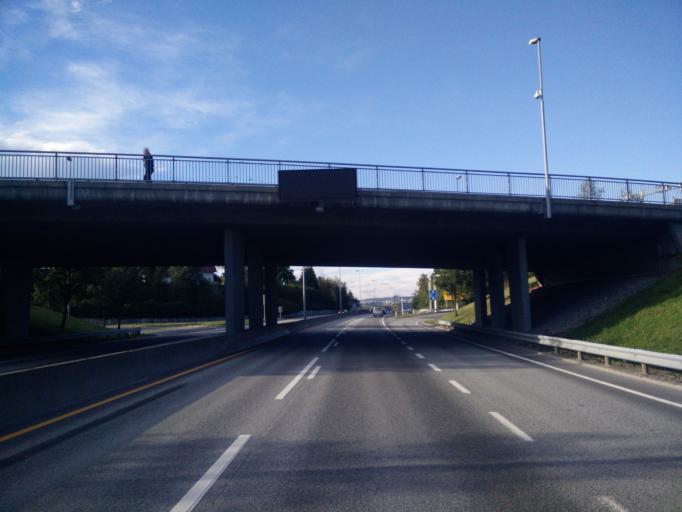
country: NO
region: Sor-Trondelag
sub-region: Trondheim
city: Trondheim
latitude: 63.4094
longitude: 10.4417
